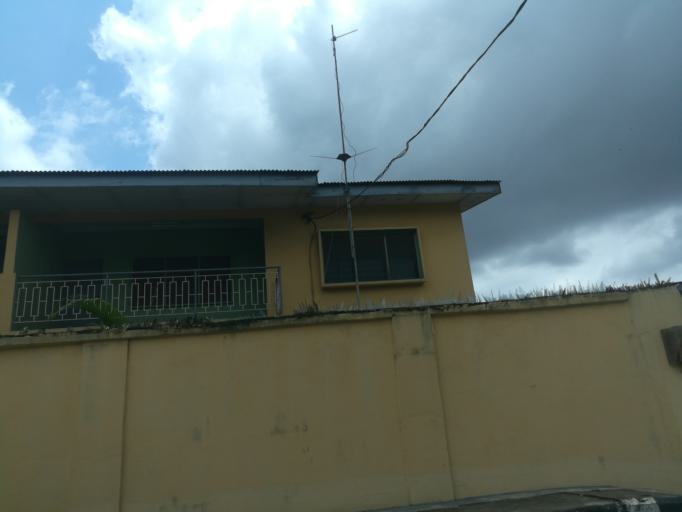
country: NG
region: Lagos
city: Somolu
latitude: 6.5513
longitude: 3.3597
